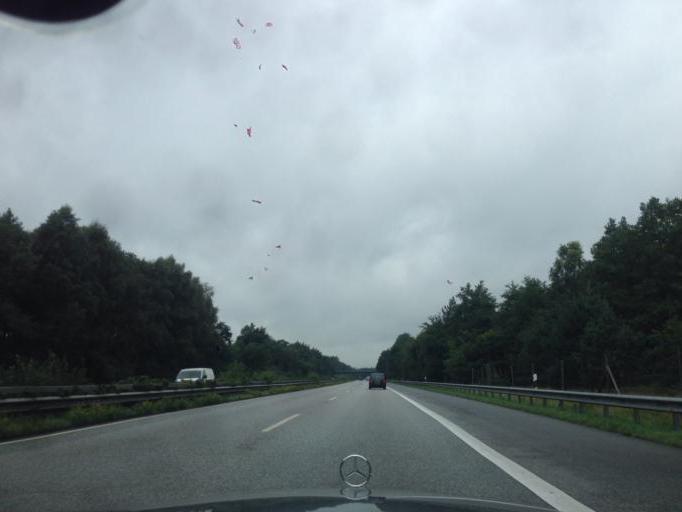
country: DE
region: Schleswig-Holstein
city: Datgen
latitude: 54.1918
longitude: 9.9163
